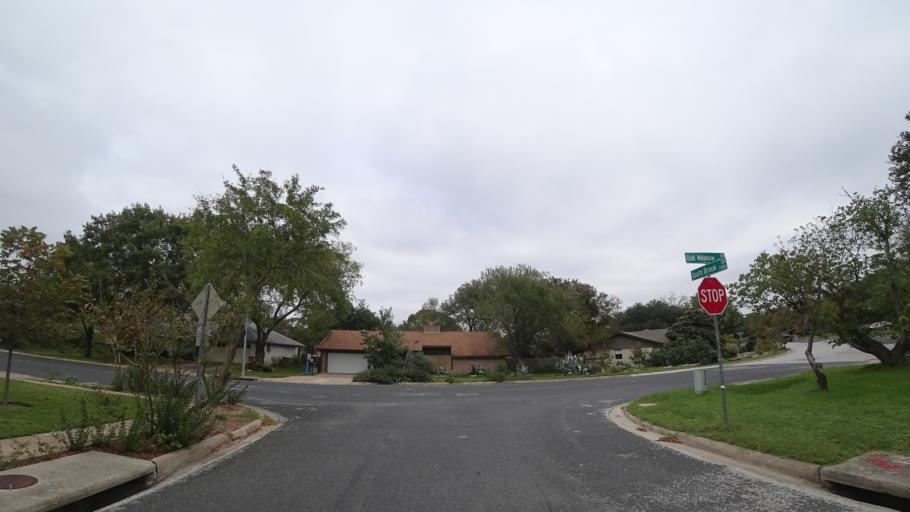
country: US
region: Texas
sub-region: Travis County
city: Barton Creek
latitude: 30.2352
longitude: -97.8820
